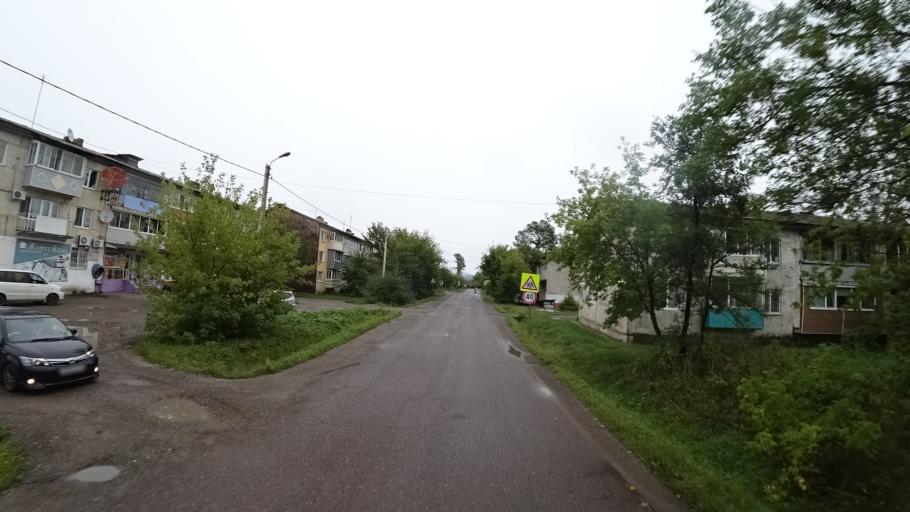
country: RU
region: Primorskiy
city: Monastyrishche
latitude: 44.2034
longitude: 132.4569
